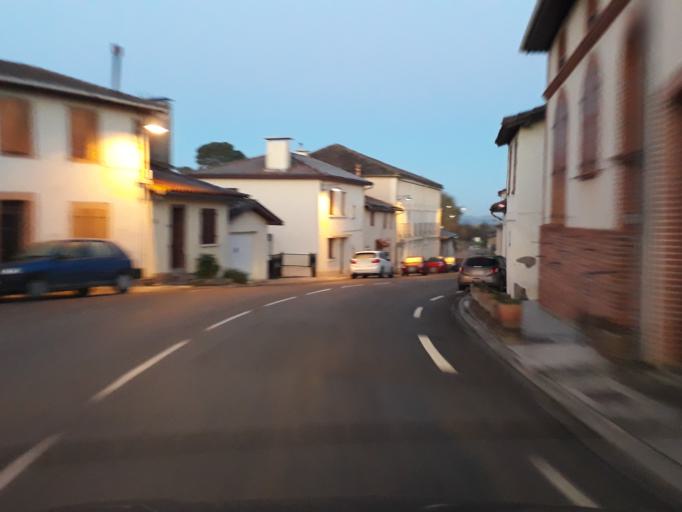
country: FR
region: Midi-Pyrenees
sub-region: Departement du Gers
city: Samatan
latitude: 43.4639
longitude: 0.9908
